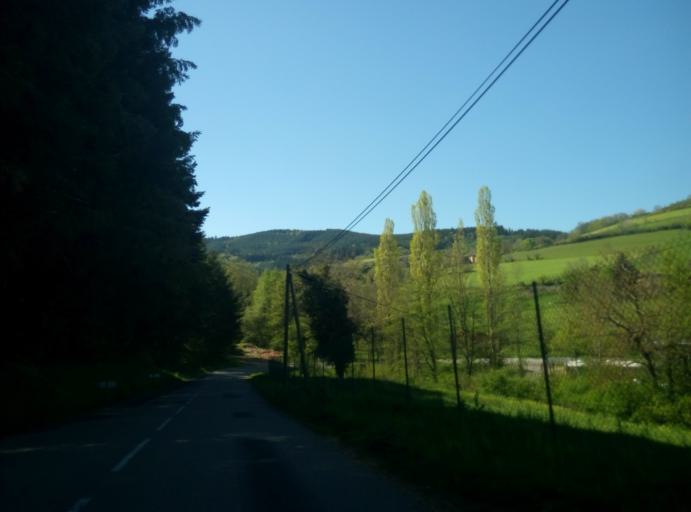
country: FR
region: Rhone-Alpes
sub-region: Departement du Rhone
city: Grandris
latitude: 46.0048
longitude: 4.4500
